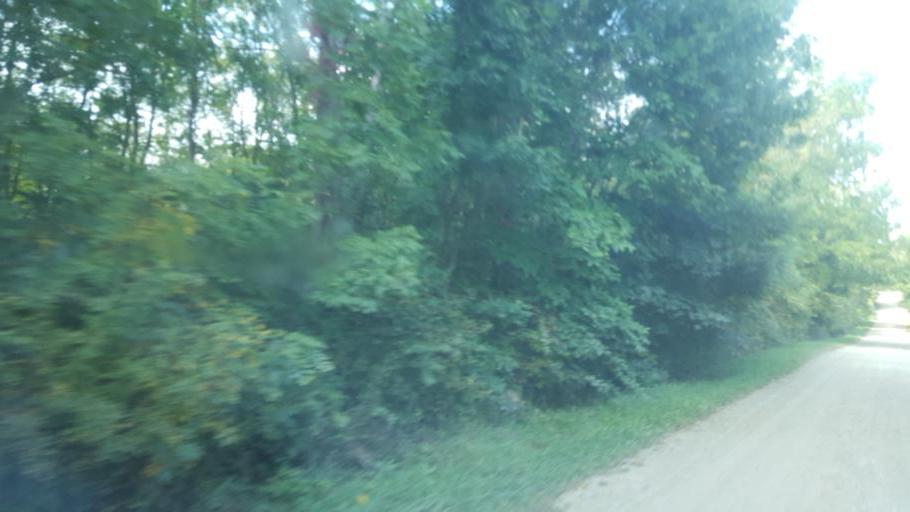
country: US
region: Ohio
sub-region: Knox County
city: Centerburg
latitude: 40.3954
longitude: -82.6307
